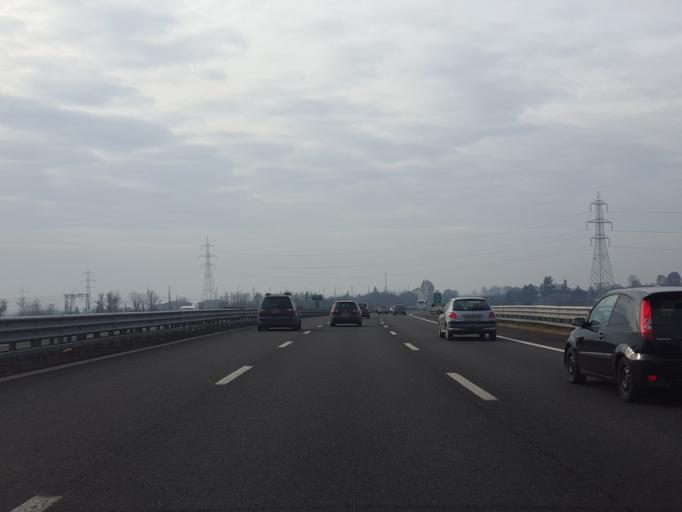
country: IT
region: Veneto
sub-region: Provincia di Vicenza
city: Montebello Vicentino
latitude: 45.4579
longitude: 11.4000
